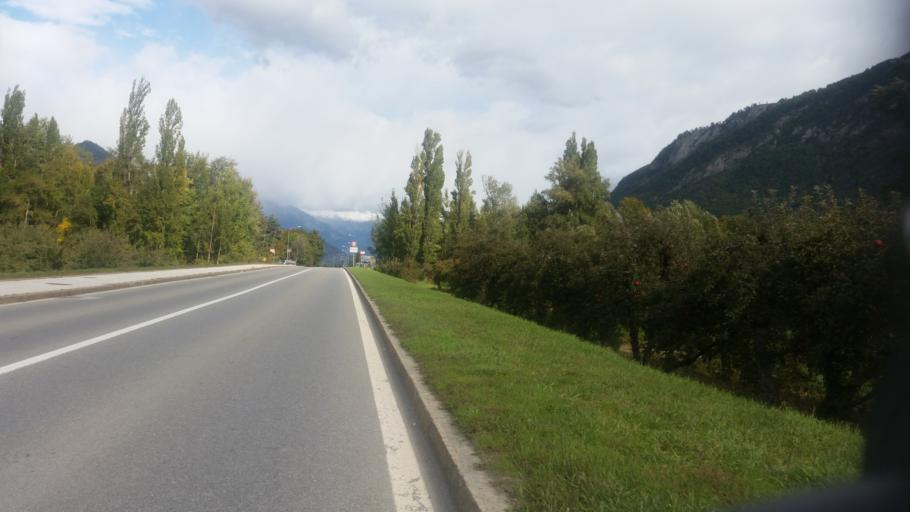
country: CH
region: Valais
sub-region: Herens District
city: Vex
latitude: 46.2324
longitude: 7.3923
